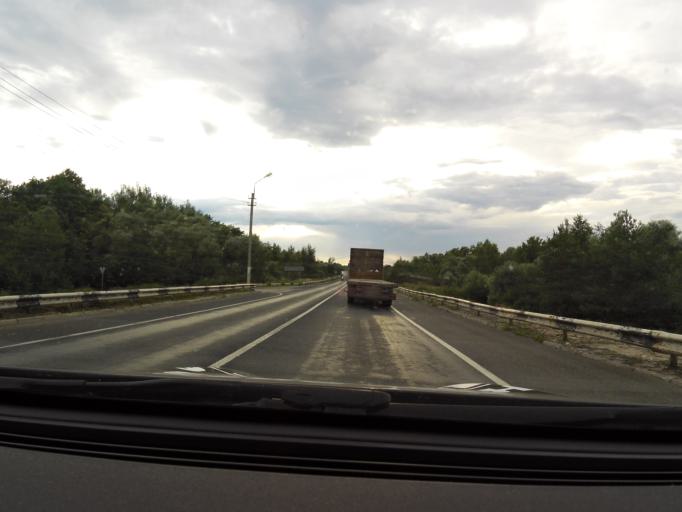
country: RU
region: Vladimir
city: Kommunar
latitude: 56.0566
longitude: 40.3964
